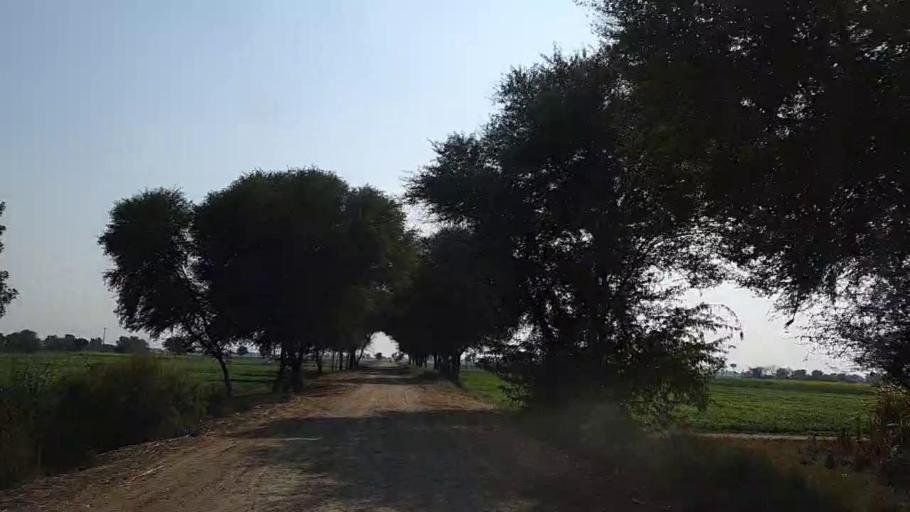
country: PK
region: Sindh
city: Daur
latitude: 26.4491
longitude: 68.2347
